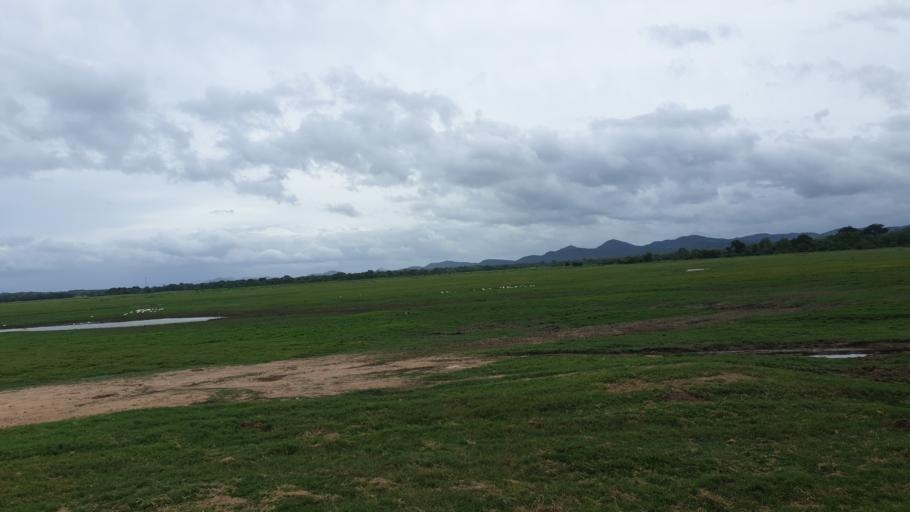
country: LK
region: North Central
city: Polonnaruwa
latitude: 8.1290
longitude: 80.9079
